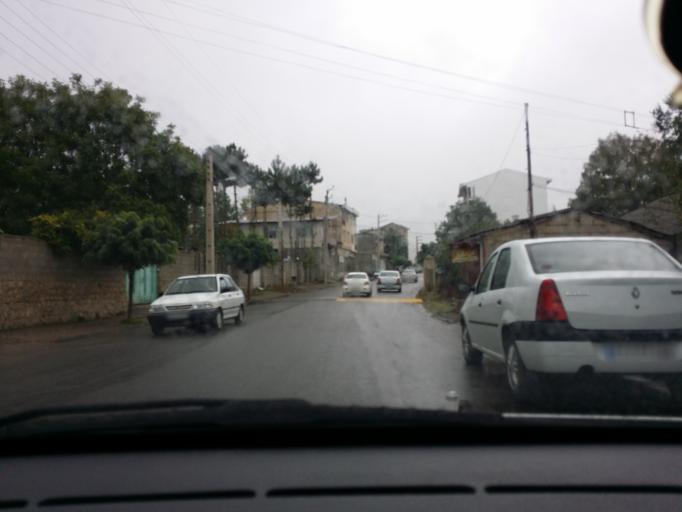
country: IR
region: Mazandaran
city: Chalus
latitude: 36.5260
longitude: 51.2319
